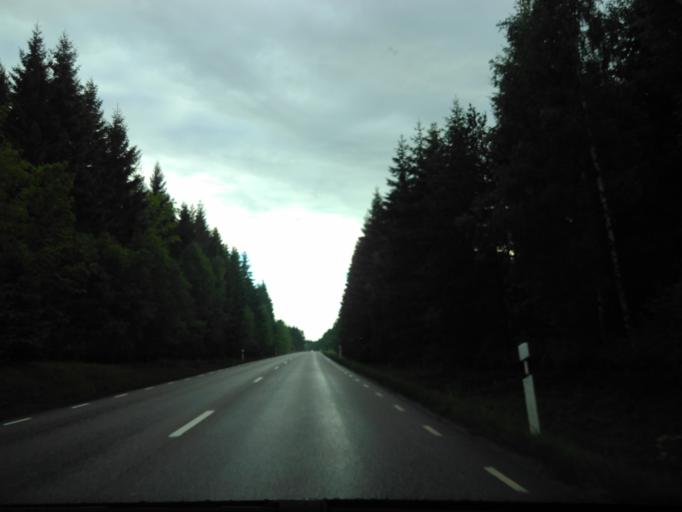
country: SE
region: Vaestra Goetaland
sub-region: Herrljunga Kommun
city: Herrljunga
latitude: 58.1026
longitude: 13.1688
